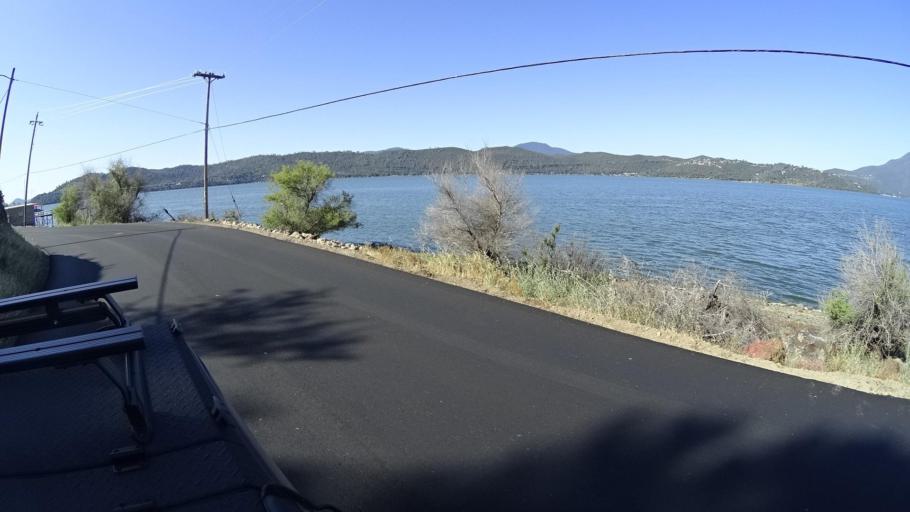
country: US
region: California
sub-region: Lake County
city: Clearlake
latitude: 38.9715
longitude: -122.6714
